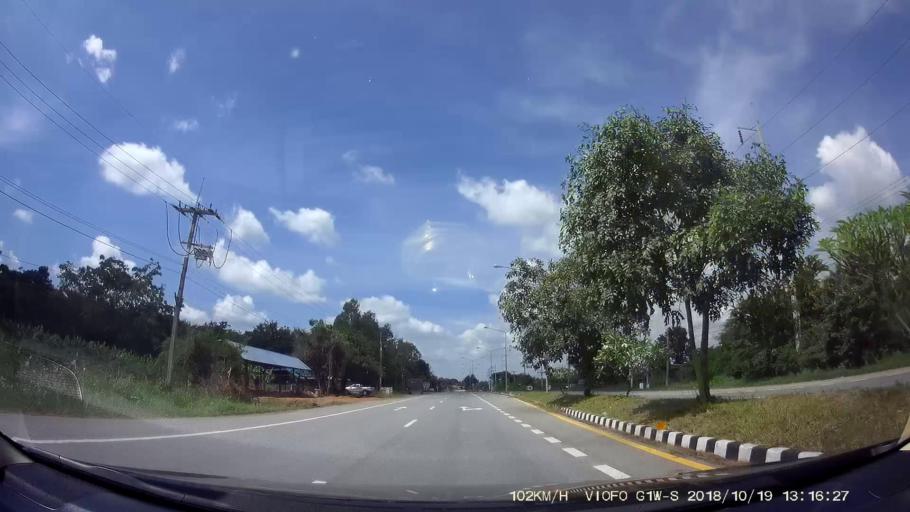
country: TH
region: Chaiyaphum
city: Chatturat
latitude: 15.4040
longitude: 101.8360
